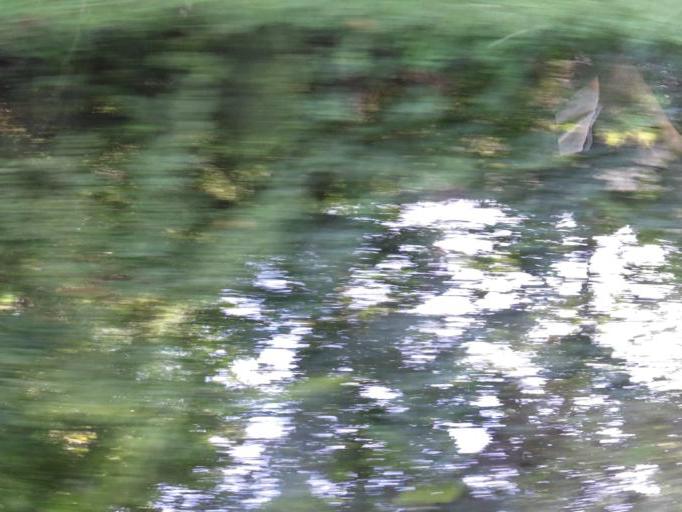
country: US
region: Florida
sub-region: Duval County
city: Jacksonville
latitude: 30.4161
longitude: -81.7328
